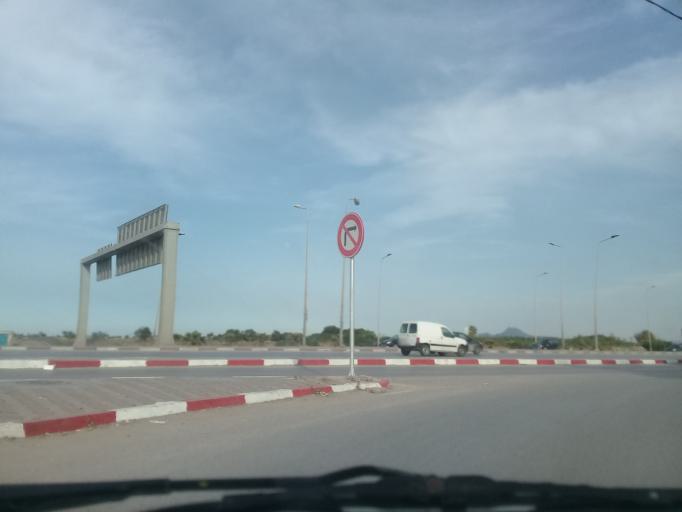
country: TN
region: Tunis
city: Tunis
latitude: 36.7934
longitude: 10.1901
